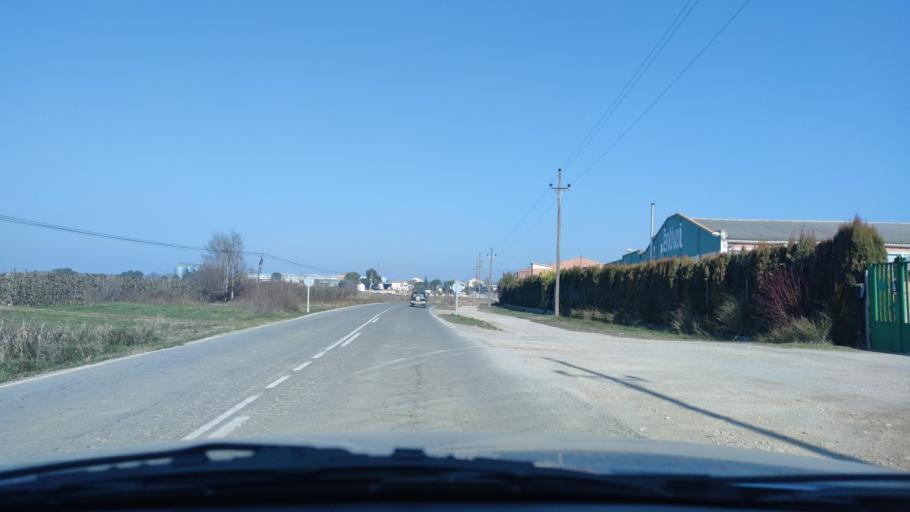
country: ES
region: Catalonia
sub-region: Provincia de Lleida
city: Aspa
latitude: 41.5474
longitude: 0.7349
